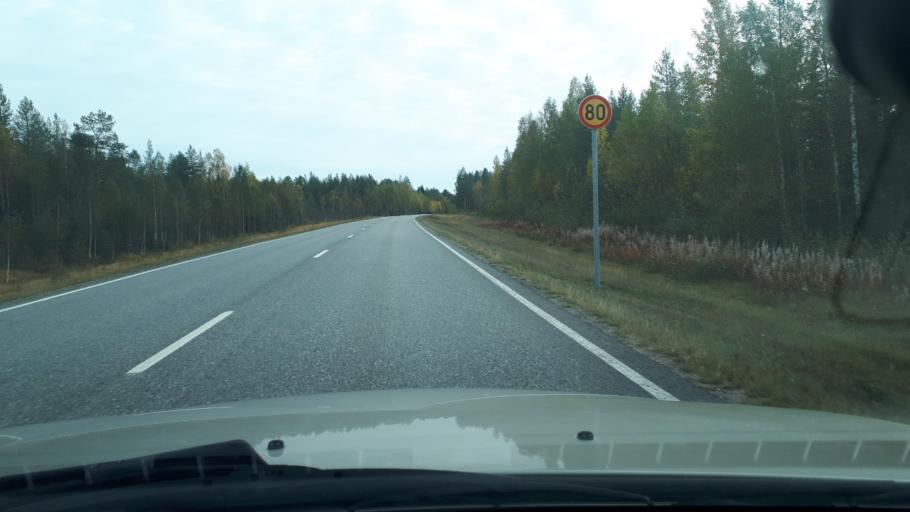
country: FI
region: Lapland
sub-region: Rovaniemi
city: Ranua
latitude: 65.9462
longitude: 26.4539
